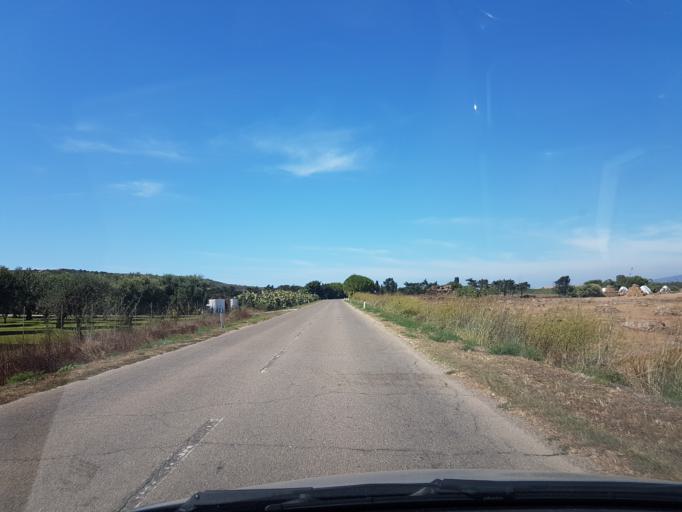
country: IT
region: Sardinia
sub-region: Provincia di Oristano
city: Cabras
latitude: 39.9411
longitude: 8.4577
